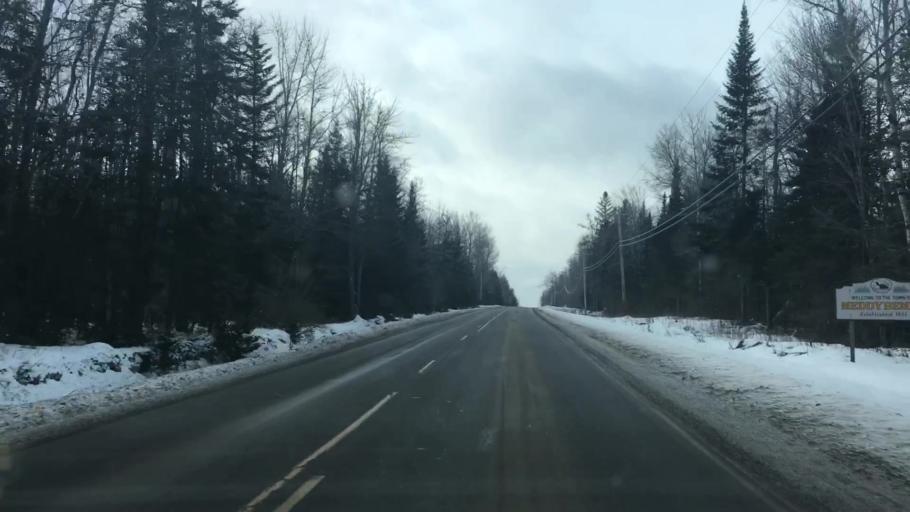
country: US
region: Maine
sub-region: Washington County
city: Calais
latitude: 45.0400
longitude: -67.3302
